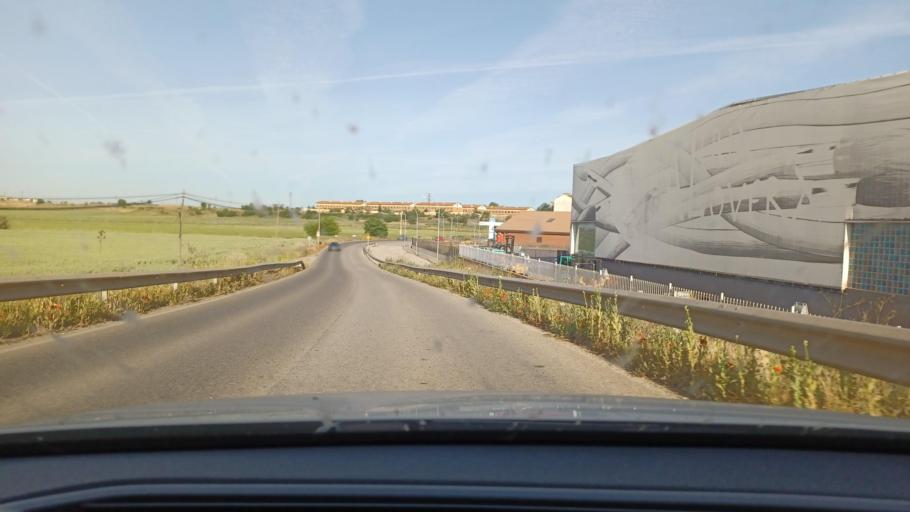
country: ES
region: Castille-La Mancha
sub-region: Provincia de Guadalajara
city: Alovera
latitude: 40.5933
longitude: -3.2335
